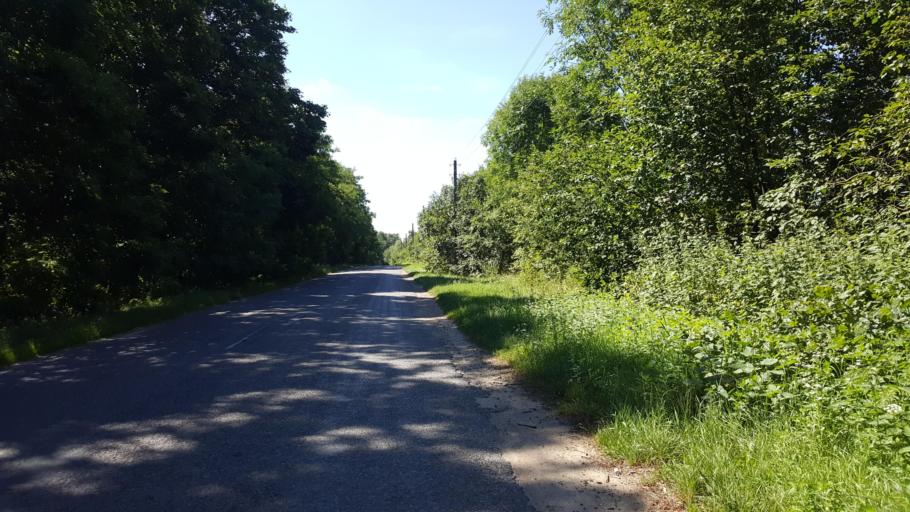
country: BY
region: Brest
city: Charnawchytsy
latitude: 52.3606
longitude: 23.6219
